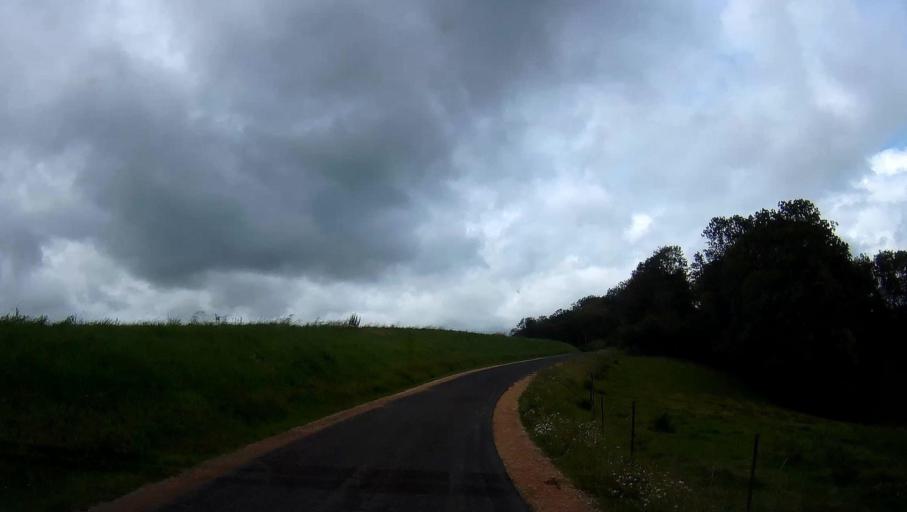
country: FR
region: Champagne-Ardenne
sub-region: Departement des Ardennes
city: Rimogne
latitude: 49.7572
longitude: 4.5316
